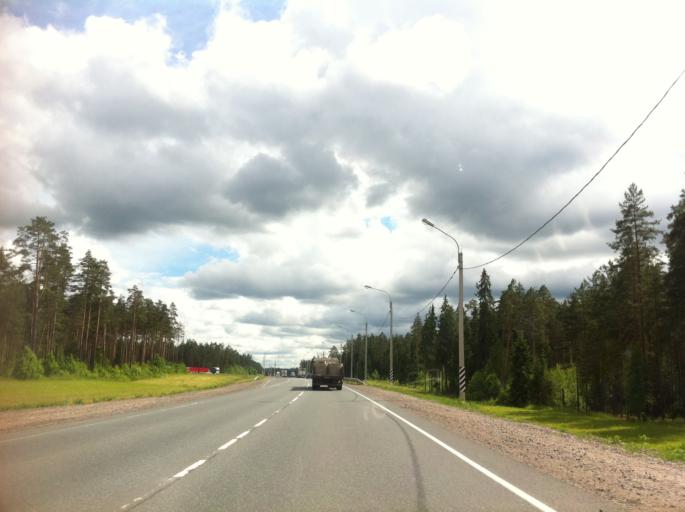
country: RU
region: Leningrad
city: Luga
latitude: 58.7192
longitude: 29.8774
